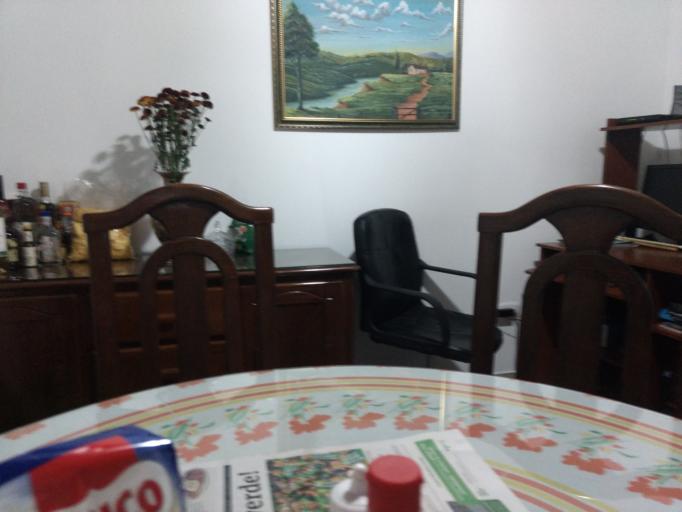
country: CO
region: Antioquia
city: Medellin
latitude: 6.2404
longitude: -75.5534
